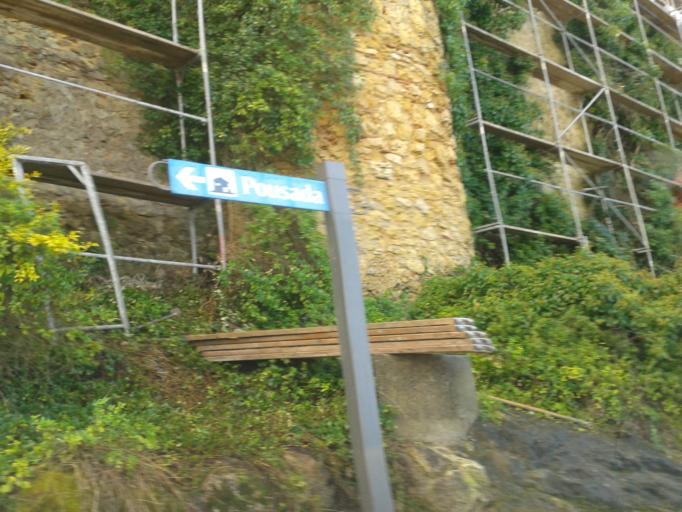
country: PT
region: Setubal
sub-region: Palmela
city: Palmela
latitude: 38.5660
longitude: -8.9017
